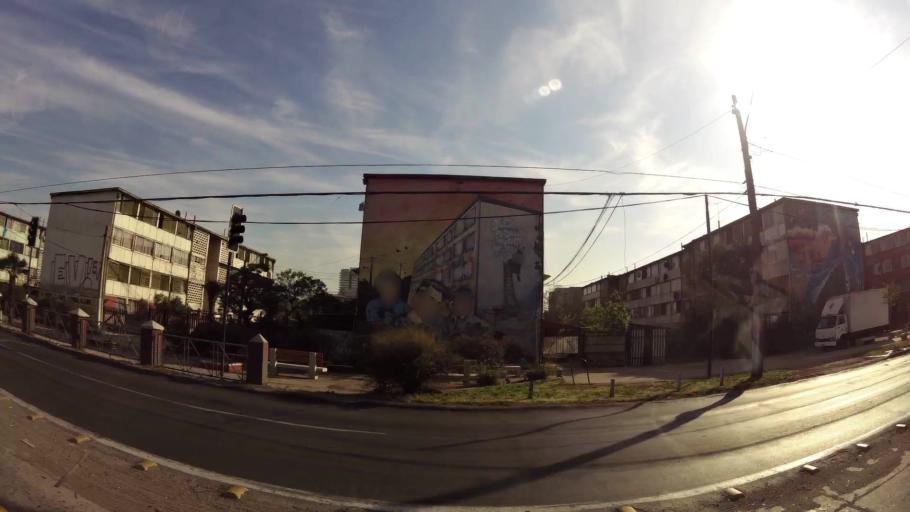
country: CL
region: Santiago Metropolitan
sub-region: Provincia de Santiago
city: Santiago
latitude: -33.5013
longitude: -70.6623
